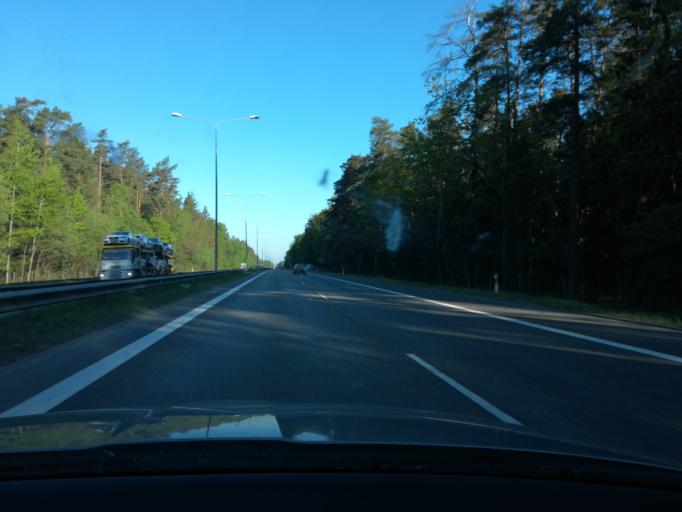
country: LT
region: Kauno apskritis
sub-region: Kauno rajonas
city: Karmelava
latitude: 54.8910
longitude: 24.1640
